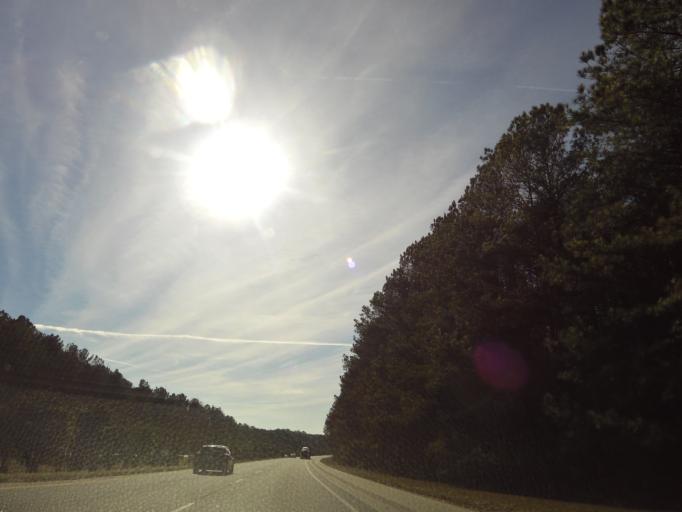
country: US
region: Georgia
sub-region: Harris County
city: Hamilton
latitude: 32.8336
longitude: -85.0041
